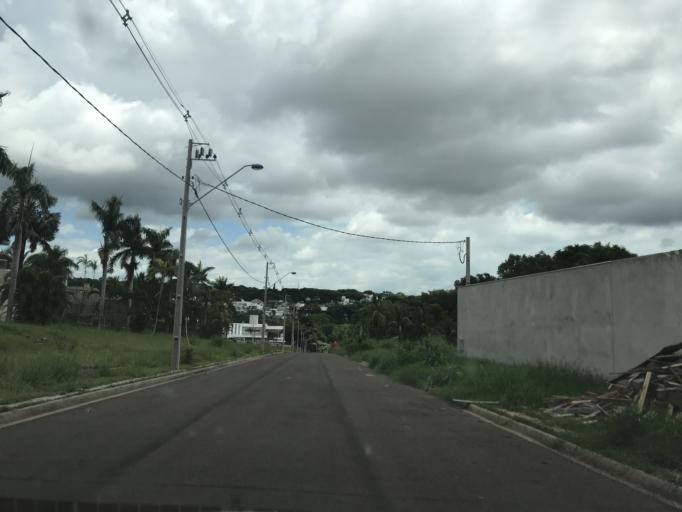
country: BR
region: Parana
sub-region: Maringa
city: Maringa
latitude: -23.4431
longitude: -51.9507
